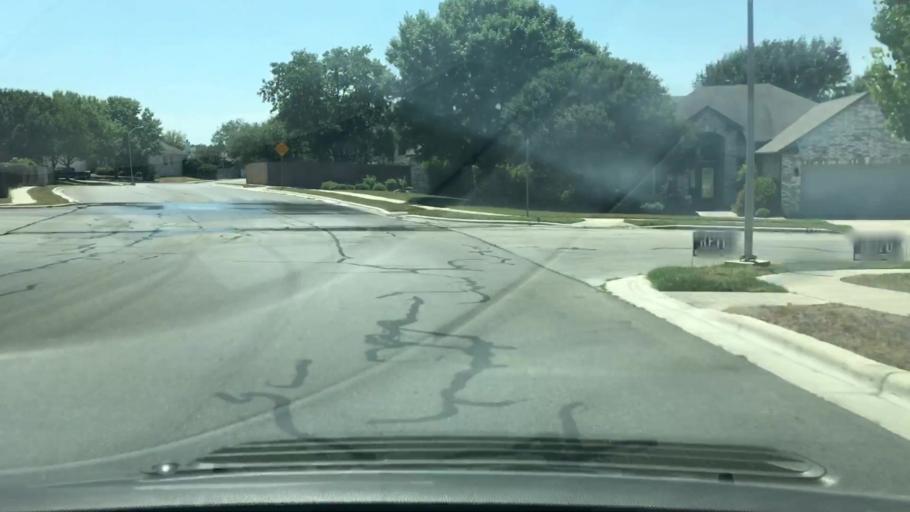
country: US
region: Texas
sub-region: Guadalupe County
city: Cibolo
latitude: 29.5827
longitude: -98.2518
